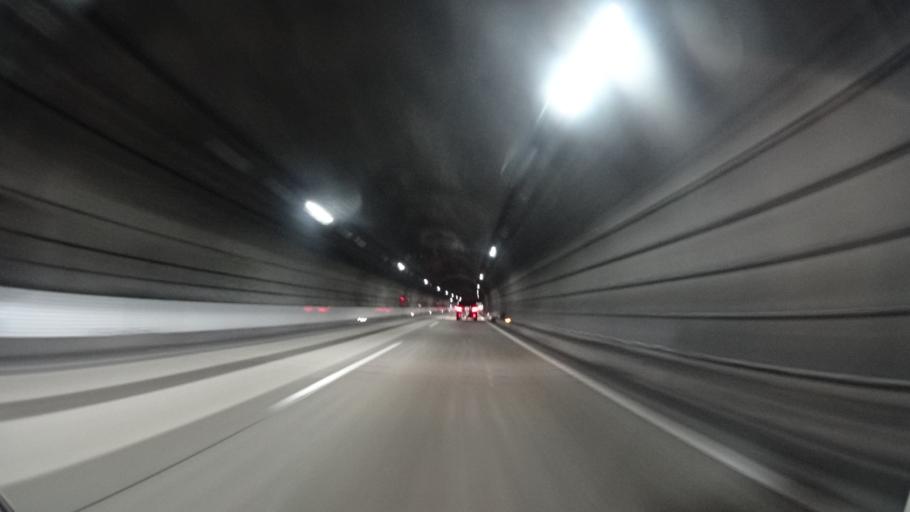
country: JP
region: Hyogo
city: Himeji
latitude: 34.8741
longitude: 134.6921
